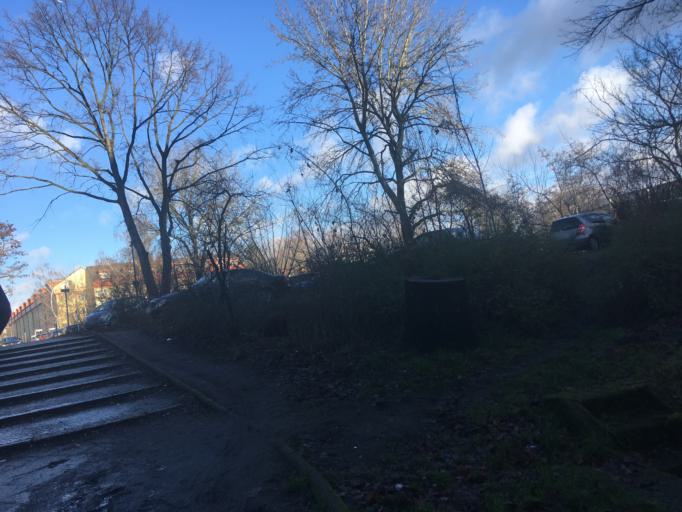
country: DE
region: Berlin
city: Reinickendorf
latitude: 52.5730
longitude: 13.3230
